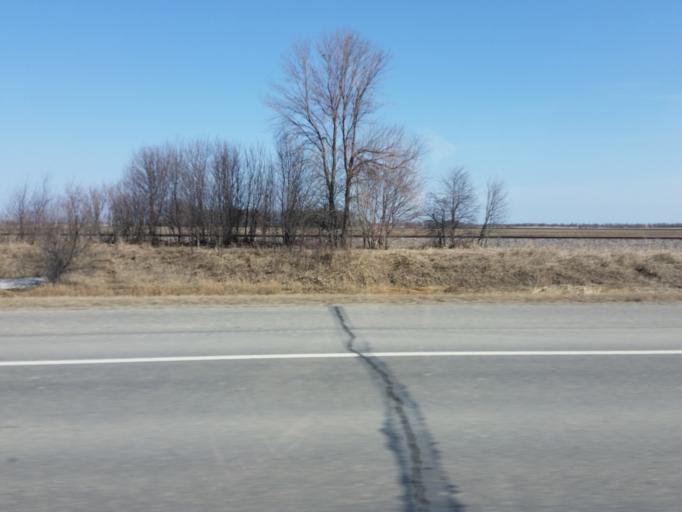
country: US
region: North Dakota
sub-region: Walsh County
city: Grafton
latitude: 48.2784
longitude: -97.3668
